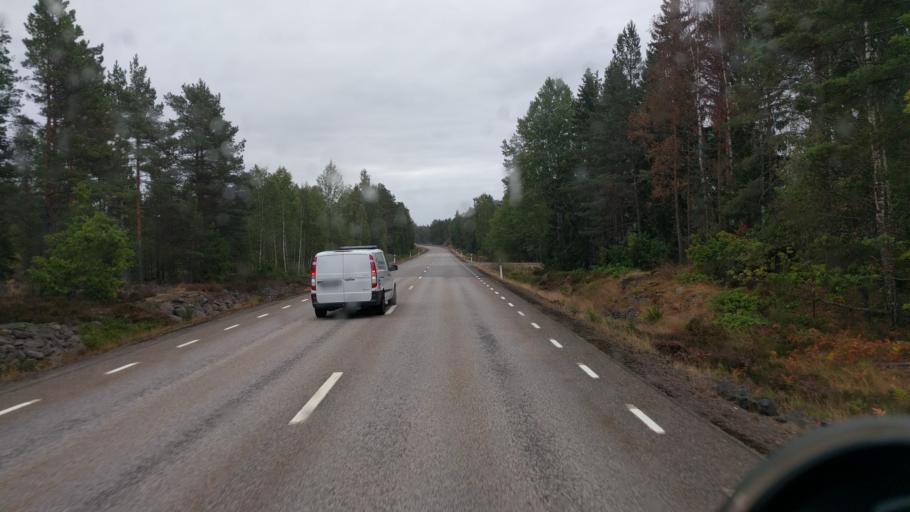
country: SE
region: Kalmar
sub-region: Vasterviks Kommun
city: Ankarsrum
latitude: 57.7029
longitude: 16.2155
